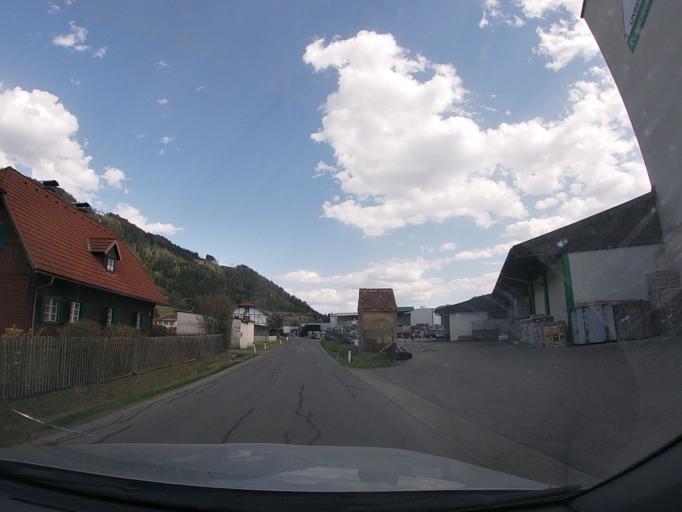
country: AT
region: Styria
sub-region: Politischer Bezirk Murtal
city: Sankt Peter ob Judenburg
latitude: 47.1945
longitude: 14.5916
